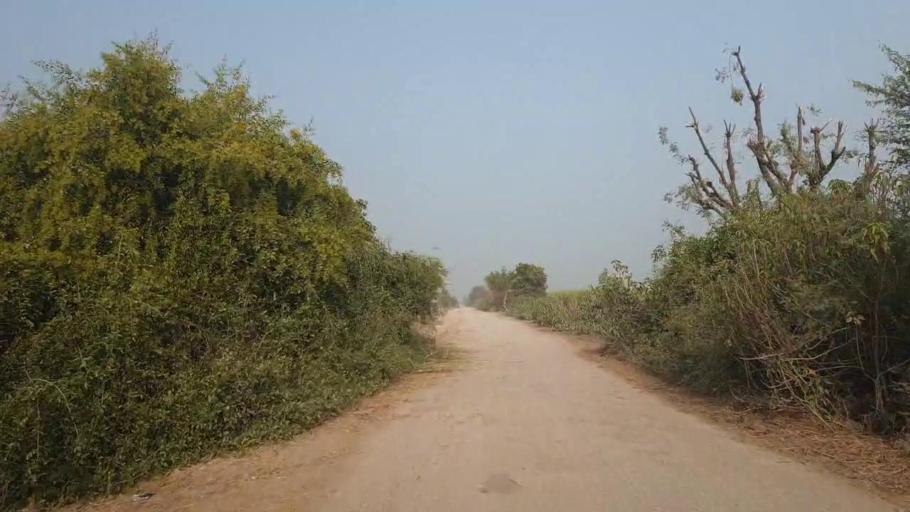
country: PK
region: Sindh
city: Shahdadpur
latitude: 25.8821
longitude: 68.5832
